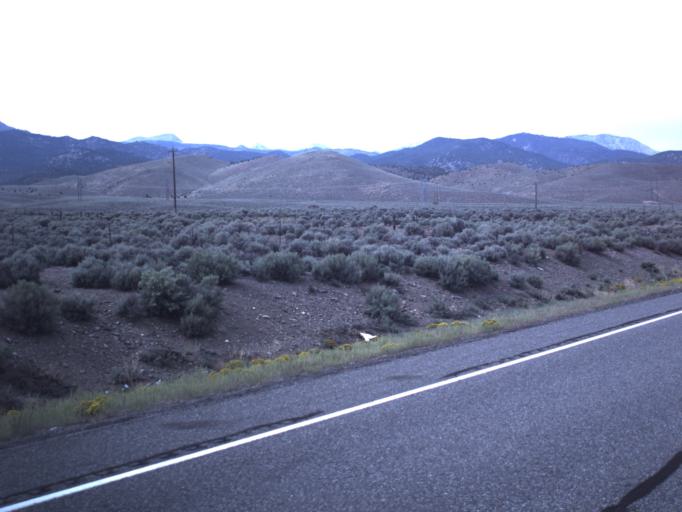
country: US
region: Utah
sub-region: Piute County
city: Junction
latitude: 38.2811
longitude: -112.2244
